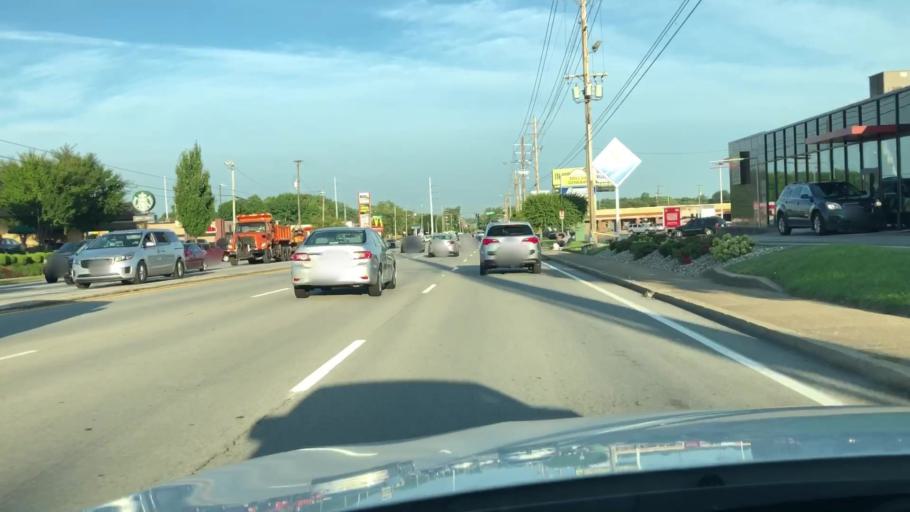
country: US
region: Kentucky
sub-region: Jefferson County
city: Saint Regis Park
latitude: 38.2200
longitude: -85.6260
